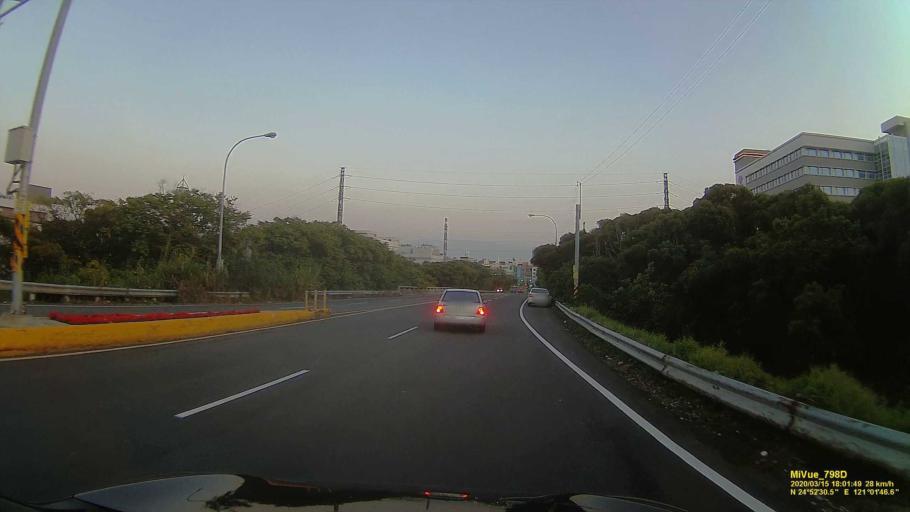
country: TW
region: Taiwan
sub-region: Hsinchu
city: Zhubei
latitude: 24.8750
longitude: 121.0297
